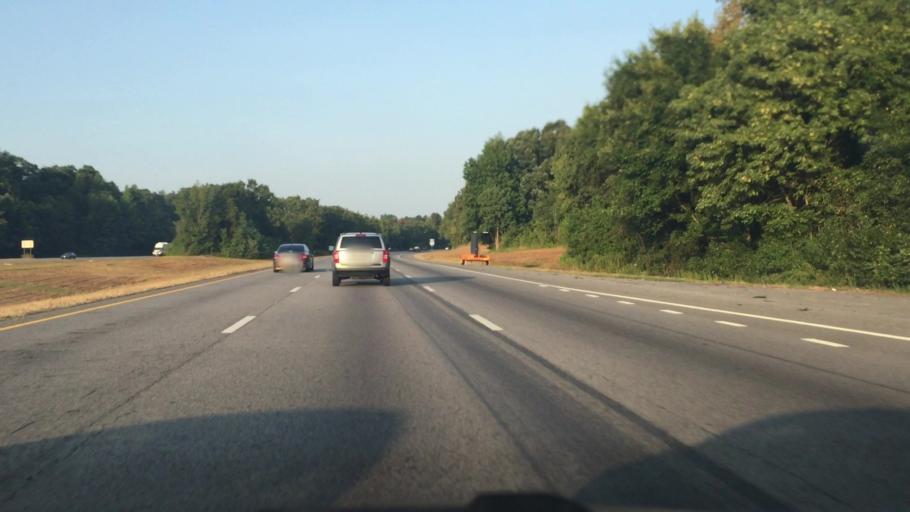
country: US
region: North Carolina
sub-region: Randolph County
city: Trinity
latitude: 35.8744
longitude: -80.0079
